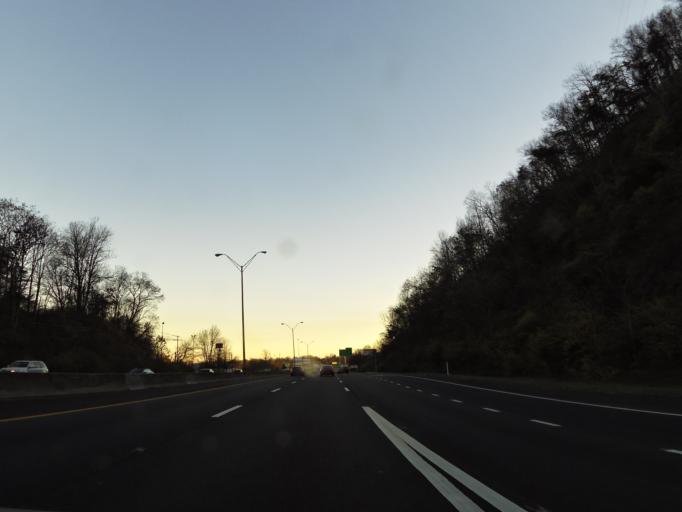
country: US
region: Tennessee
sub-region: Knox County
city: Knoxville
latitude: 35.9972
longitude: -83.9539
